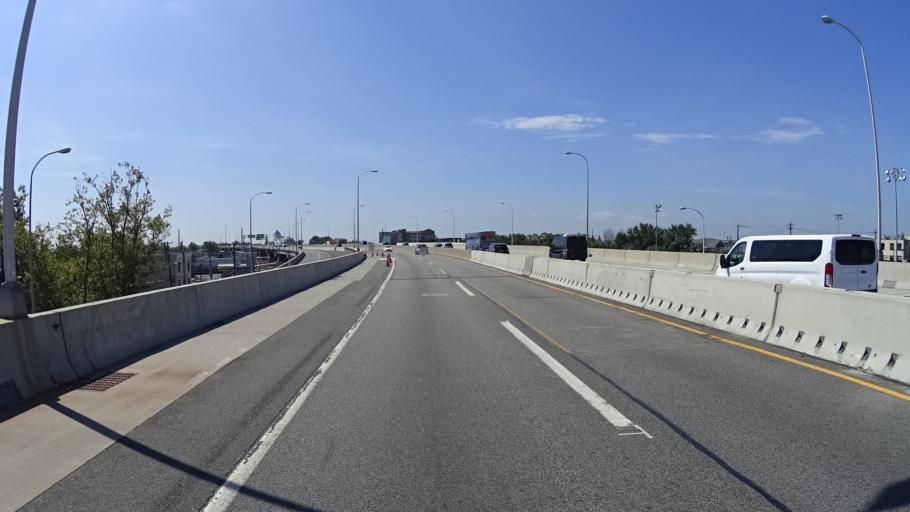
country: US
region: New Jersey
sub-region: Hudson County
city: Jersey City
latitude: 40.7185
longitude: -74.0558
